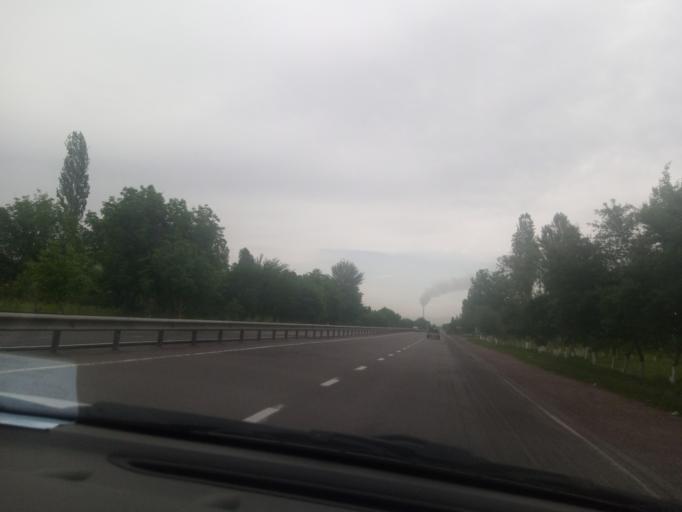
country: UZ
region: Toshkent
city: Ohangaron
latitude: 40.9005
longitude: 69.7032
